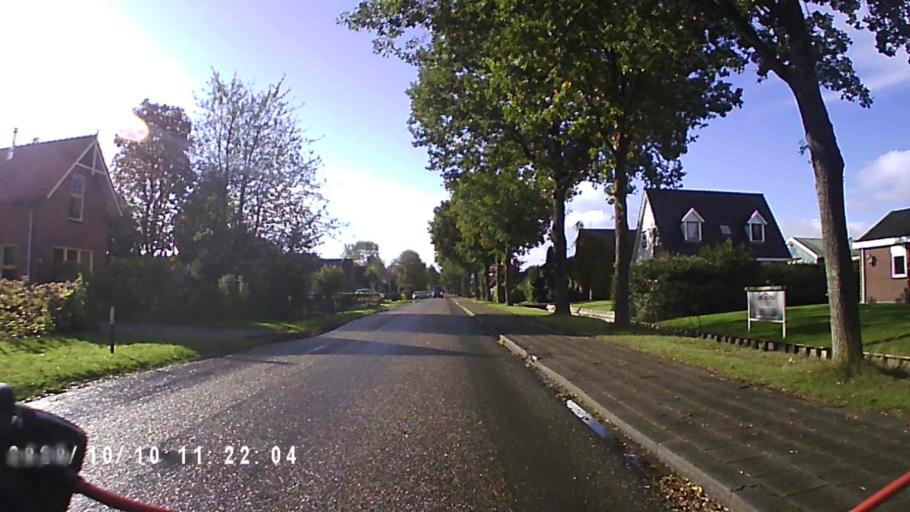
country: NL
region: Friesland
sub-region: Gemeente Smallingerland
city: Drachtstercompagnie
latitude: 53.0943
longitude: 6.1788
